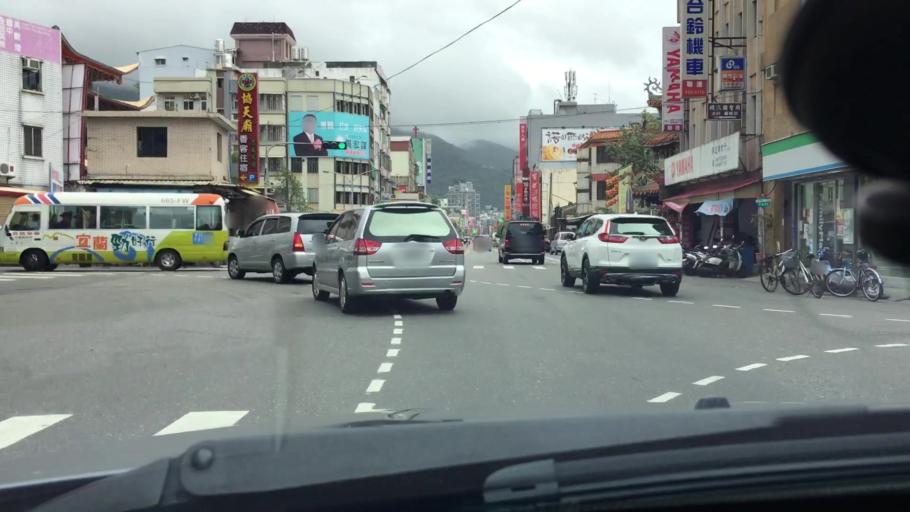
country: TW
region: Taiwan
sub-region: Yilan
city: Yilan
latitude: 24.8183
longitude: 121.7686
